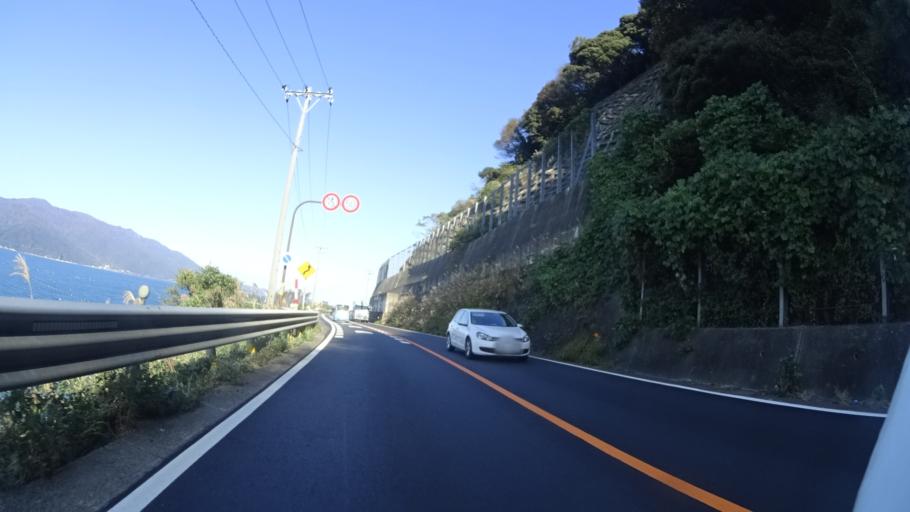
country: JP
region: Fukui
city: Tsuruga
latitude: 35.6949
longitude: 136.0813
